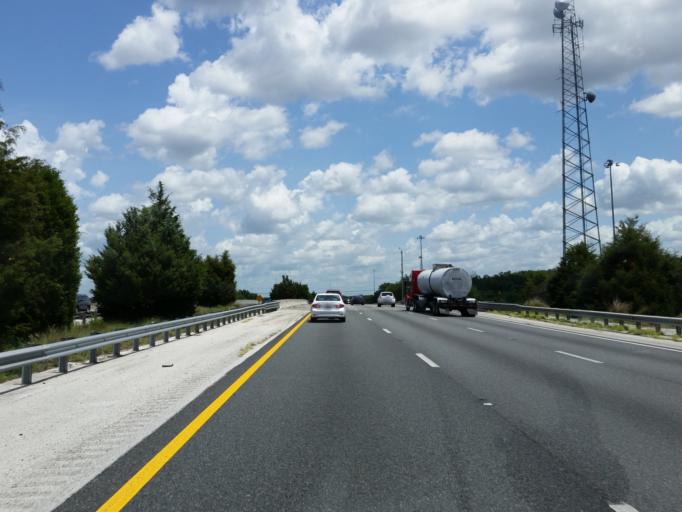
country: US
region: Florida
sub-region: Sumter County
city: Wildwood
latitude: 28.8727
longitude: -82.0922
